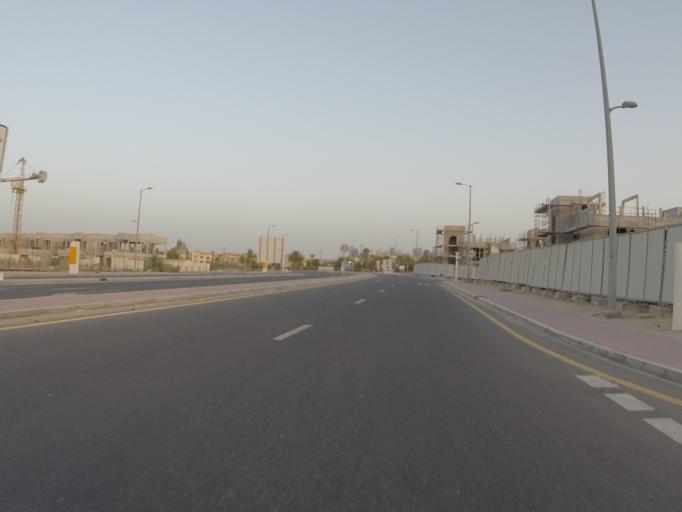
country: AE
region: Dubai
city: Dubai
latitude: 25.0486
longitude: 55.1664
